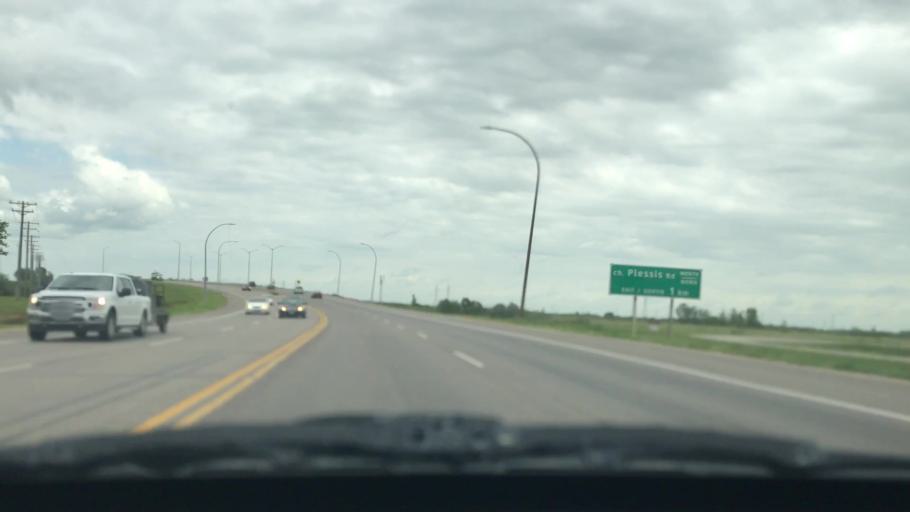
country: CA
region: Manitoba
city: Winnipeg
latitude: 49.8553
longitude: -97.0286
